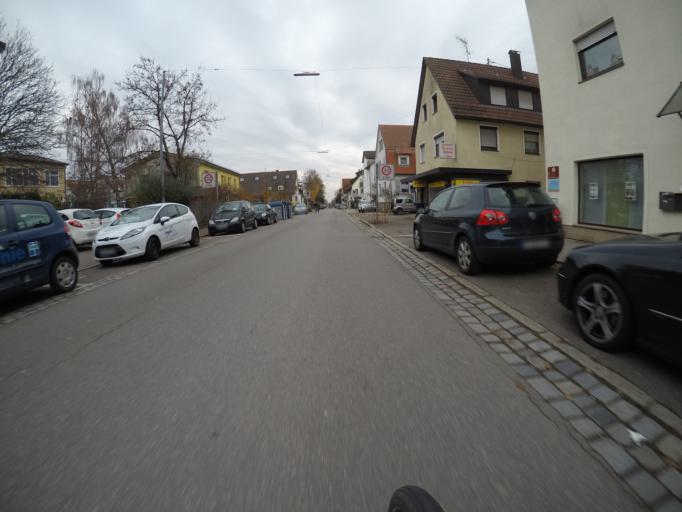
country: DE
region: Baden-Wuerttemberg
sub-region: Regierungsbezirk Stuttgart
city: Leinfelden-Echterdingen
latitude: 48.6882
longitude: 9.1698
